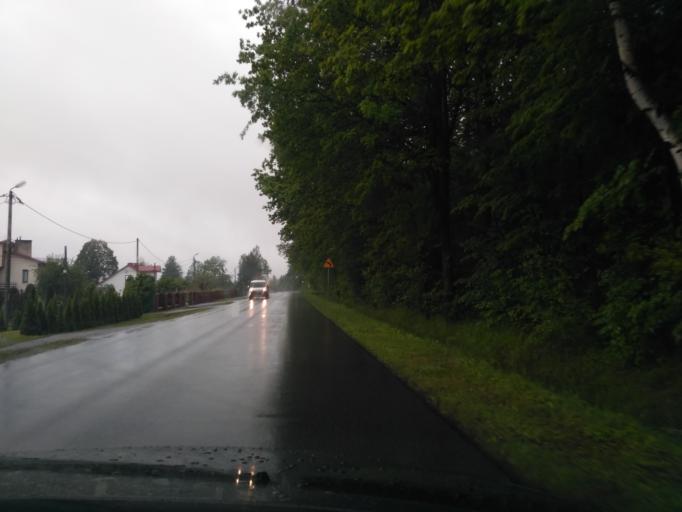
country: PL
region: Subcarpathian Voivodeship
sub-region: Powiat jasielski
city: Debowiec
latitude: 49.6541
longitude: 21.4146
